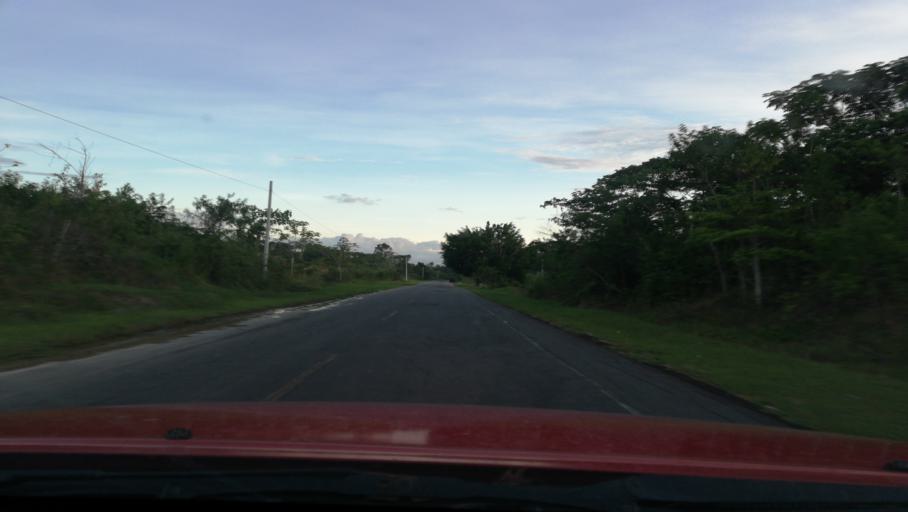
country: PE
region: Loreto
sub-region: Provincia de Loreto
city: Nauta
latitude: -4.3196
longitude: -73.5274
